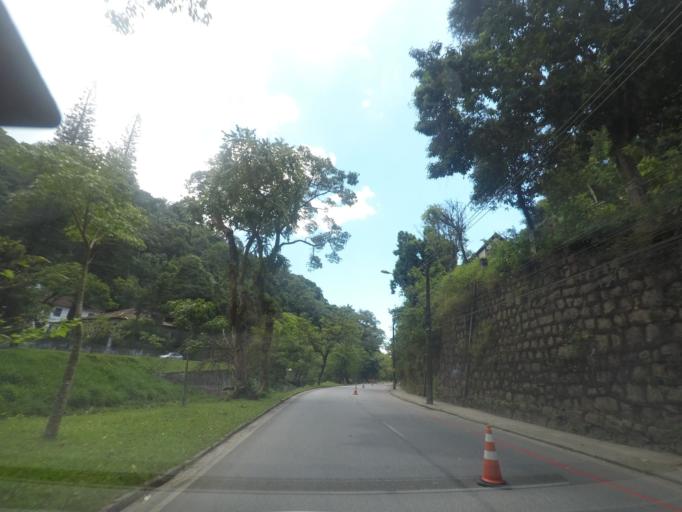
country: BR
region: Rio de Janeiro
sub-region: Petropolis
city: Petropolis
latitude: -22.5018
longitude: -43.1815
